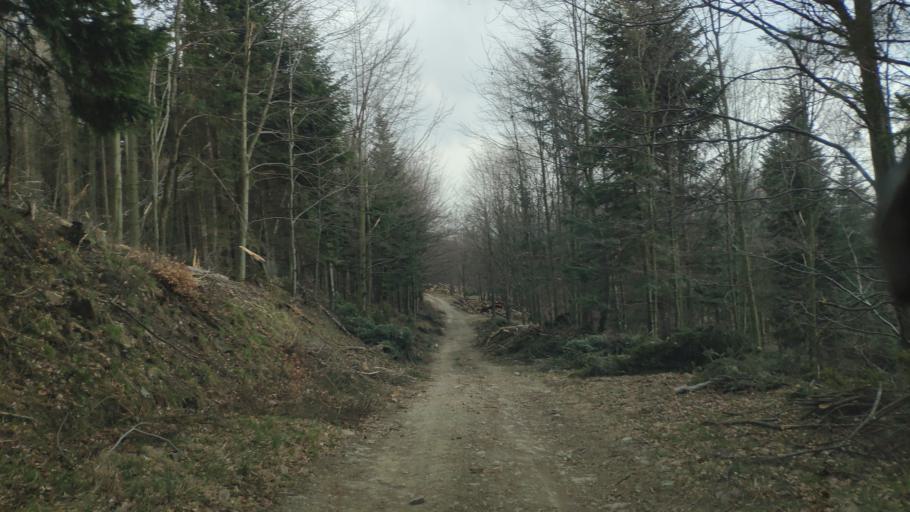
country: SK
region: Kosicky
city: Moldava nad Bodvou
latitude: 48.7465
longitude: 21.0406
